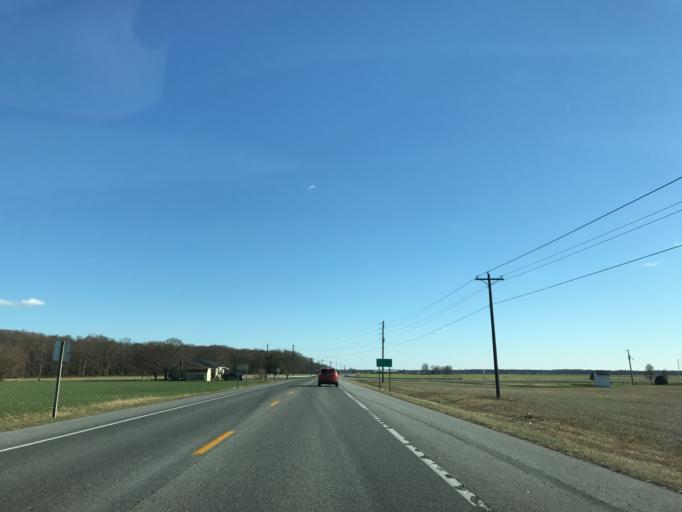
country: US
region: Maryland
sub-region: Caroline County
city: Greensboro
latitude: 39.0945
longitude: -75.8700
